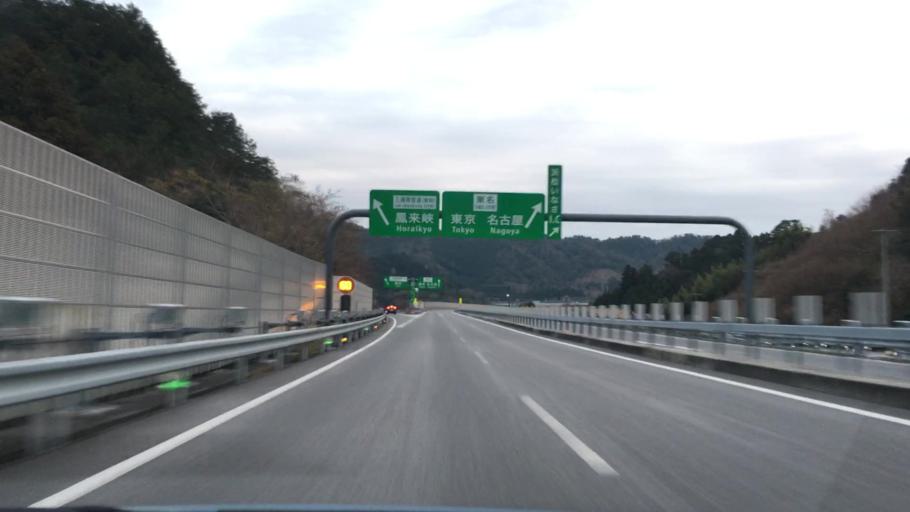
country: JP
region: Shizuoka
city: Hamakita
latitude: 34.8870
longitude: 137.6601
